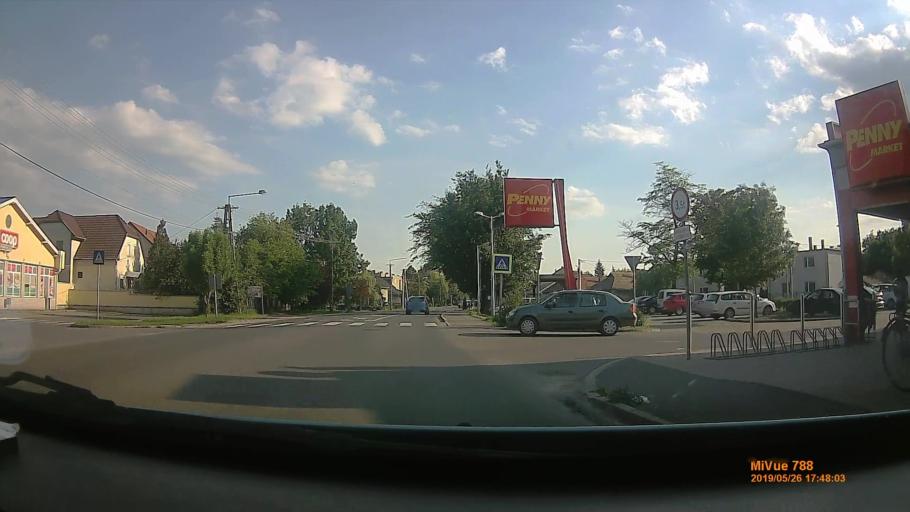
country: HU
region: Borsod-Abauj-Zemplen
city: Szikszo
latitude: 48.1979
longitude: 20.9312
